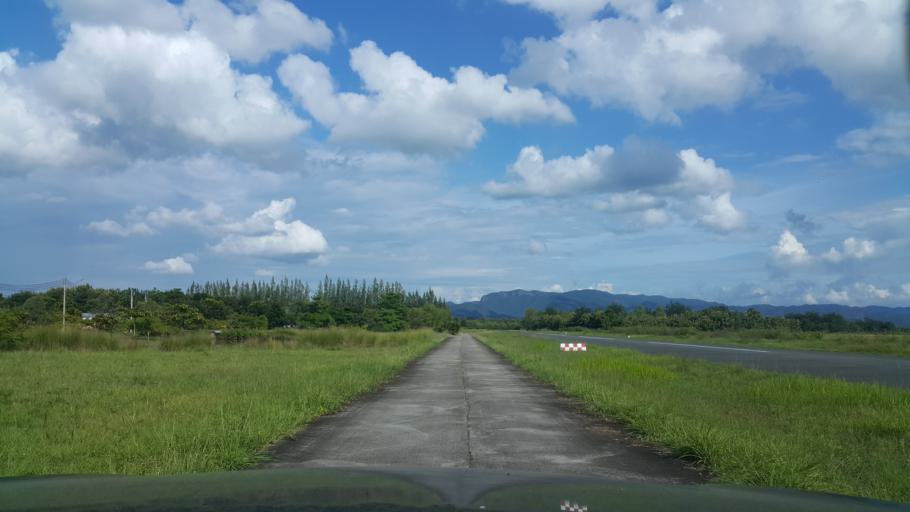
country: TH
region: Lamphun
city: Ban Thi
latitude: 18.6766
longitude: 99.1030
